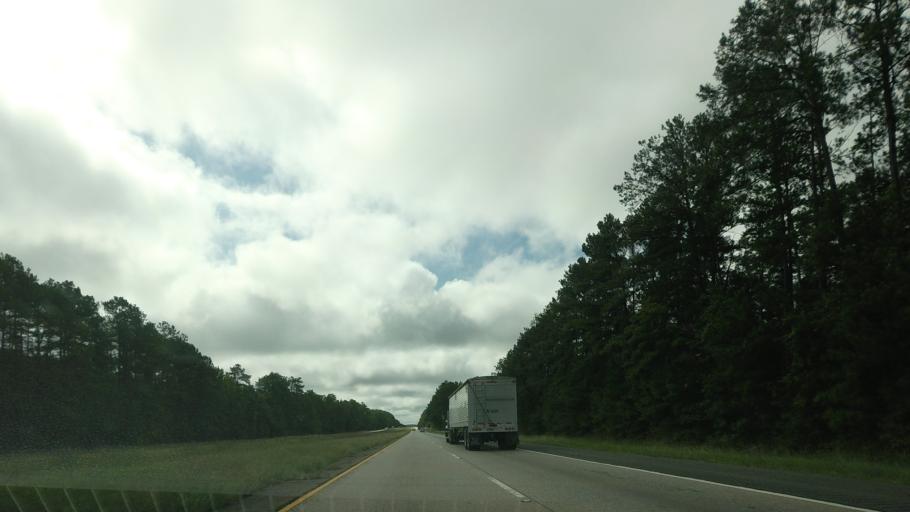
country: US
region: Georgia
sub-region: Bibb County
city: Macon
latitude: 32.7519
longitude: -83.5501
